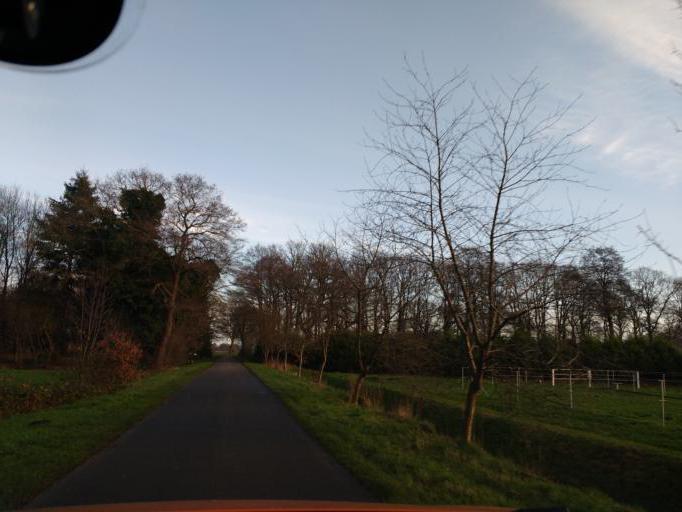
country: DE
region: Lower Saxony
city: Hatten
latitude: 53.1192
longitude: 8.3651
